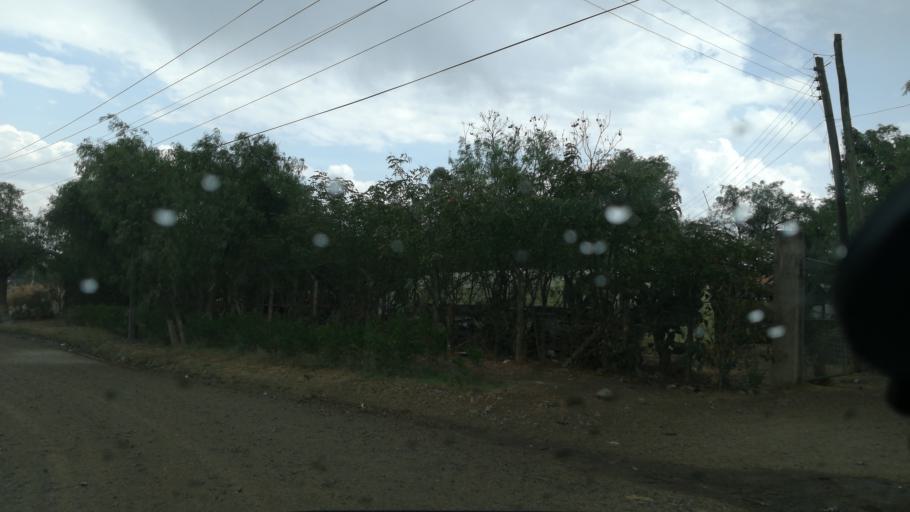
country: BO
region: Cochabamba
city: Cochabamba
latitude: -17.3376
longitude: -66.2114
